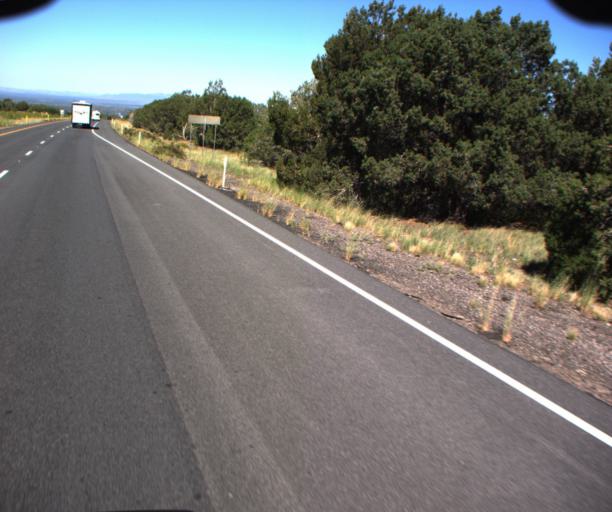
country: US
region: Arizona
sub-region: Coconino County
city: Williams
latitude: 35.2164
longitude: -112.3795
